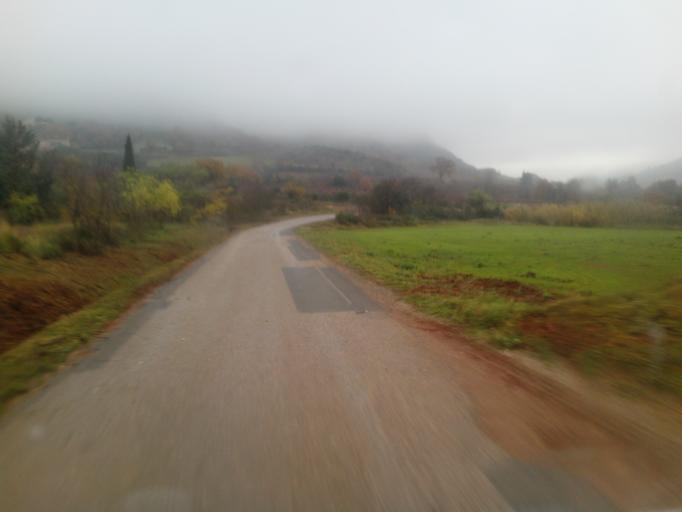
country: FR
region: Languedoc-Roussillon
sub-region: Departement de l'Herault
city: Nebian
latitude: 43.6392
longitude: 3.3594
